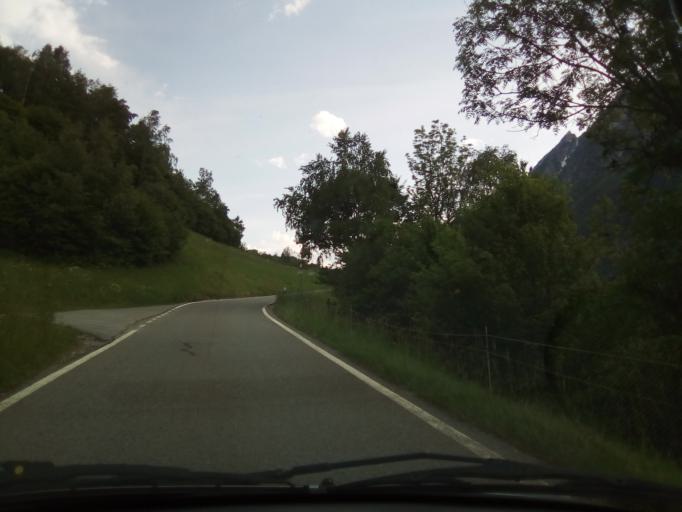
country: CH
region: Valais
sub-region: Entremont District
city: Orsieres
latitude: 46.0666
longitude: 7.1558
